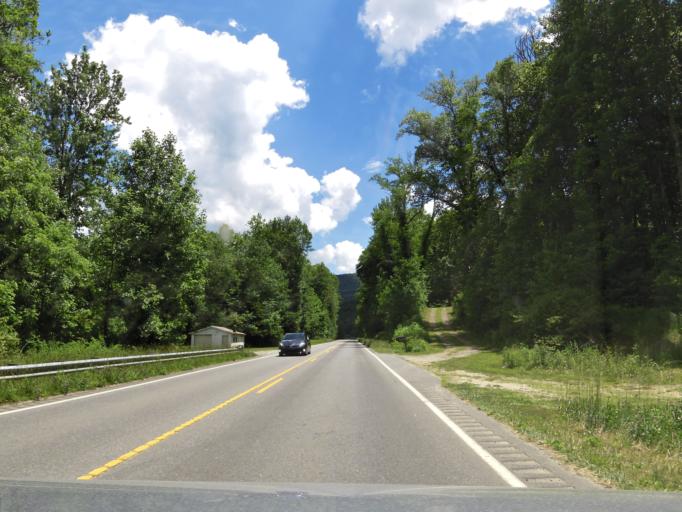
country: US
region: North Carolina
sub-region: Graham County
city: Robbinsville
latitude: 35.2828
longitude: -83.7656
